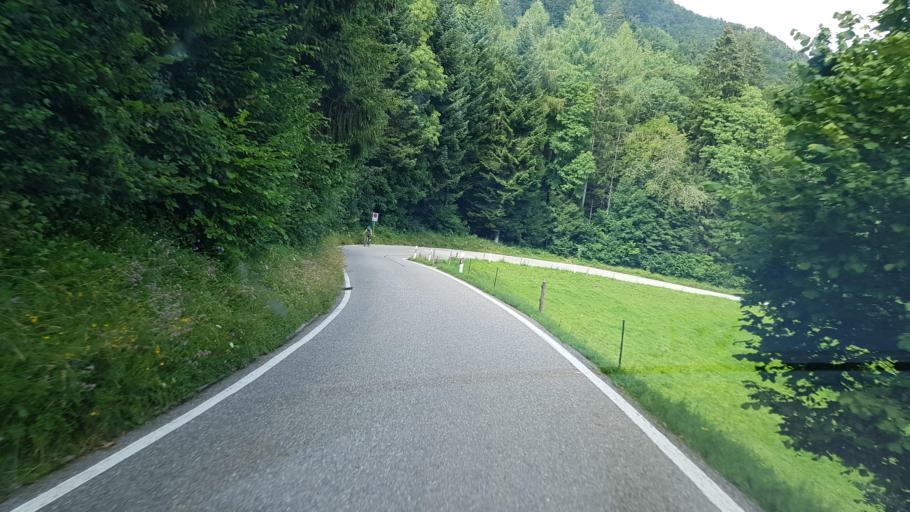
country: CH
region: Solothurn
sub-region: Bezirk Lebern
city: Riedholz
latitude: 47.2626
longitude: 7.5637
